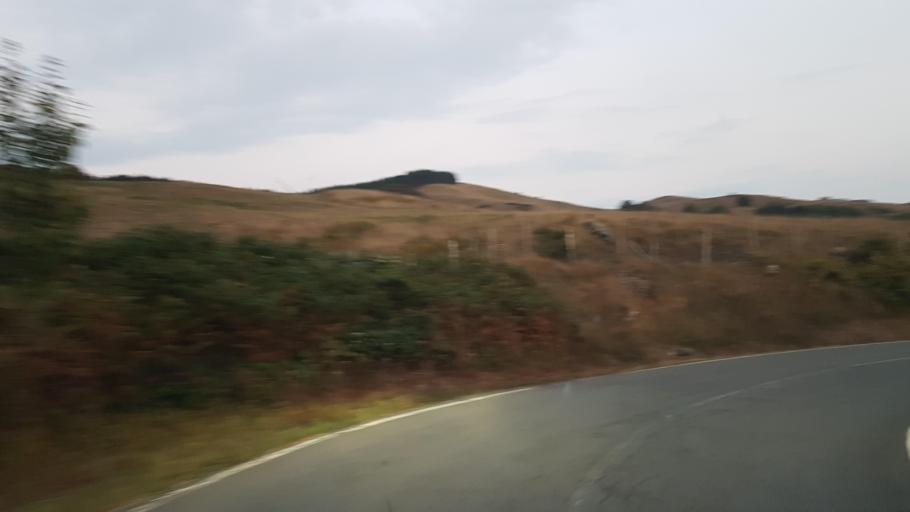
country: IT
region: Liguria
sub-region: Provincia di La Spezia
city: Varese Ligure
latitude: 44.4169
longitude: 9.6284
